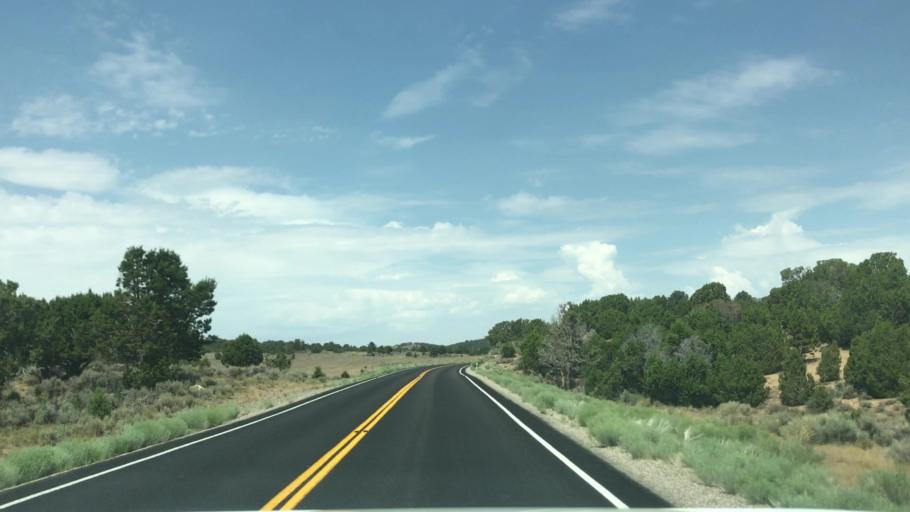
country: US
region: Nevada
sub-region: Eureka County
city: Eureka
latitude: 39.3916
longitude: -115.4554
